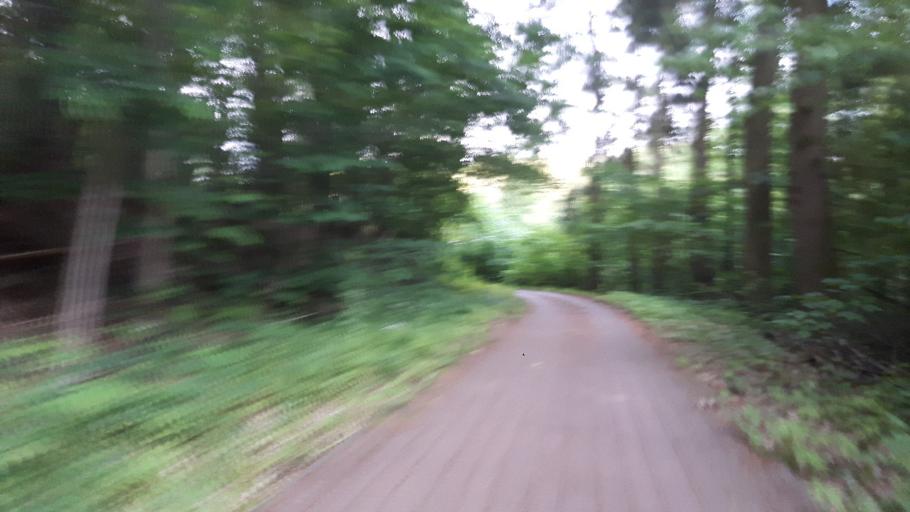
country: DE
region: Brandenburg
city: Mescherin
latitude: 53.2334
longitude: 14.4133
